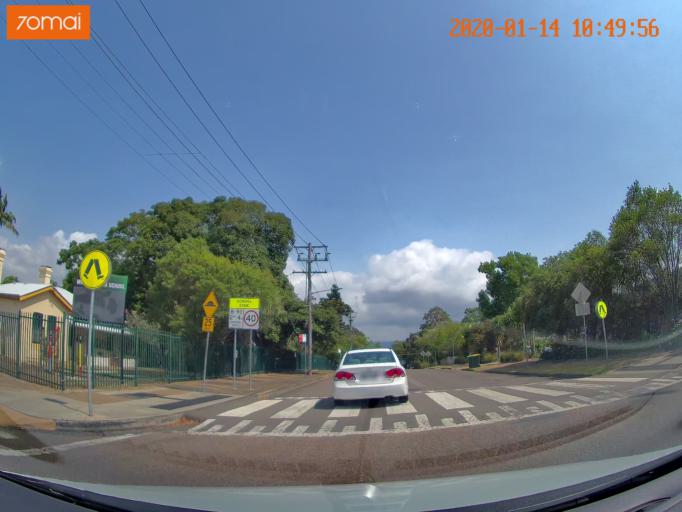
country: AU
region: New South Wales
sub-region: Lake Macquarie Shire
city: Dora Creek
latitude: -33.1057
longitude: 151.4887
